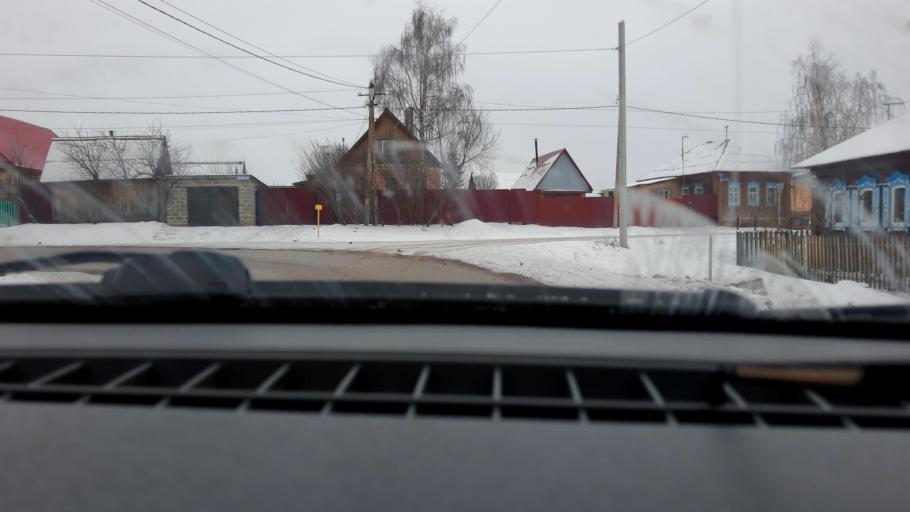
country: RU
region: Bashkortostan
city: Kabakovo
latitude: 54.7038
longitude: 56.2467
